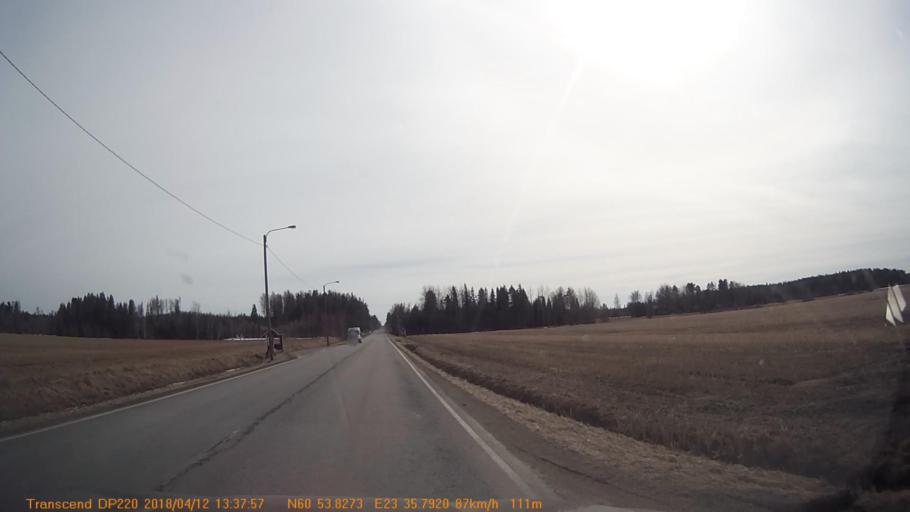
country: FI
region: Haeme
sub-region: Forssa
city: Forssa
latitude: 60.8969
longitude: 23.5966
